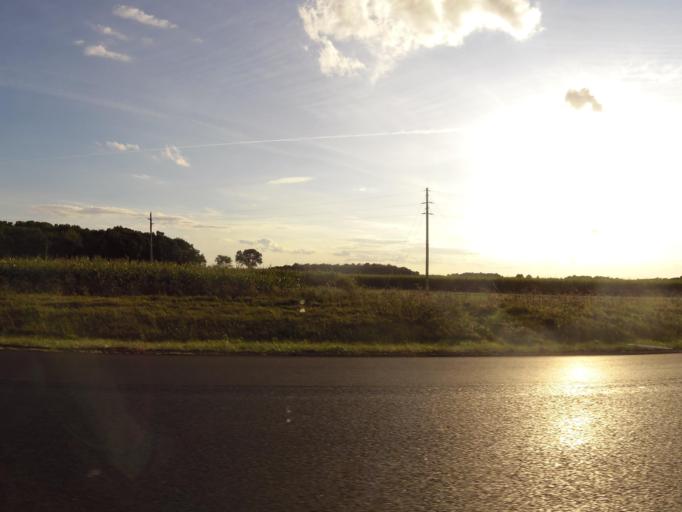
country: US
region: Indiana
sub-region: Boone County
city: Thorntown
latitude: 40.1977
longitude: -86.5744
